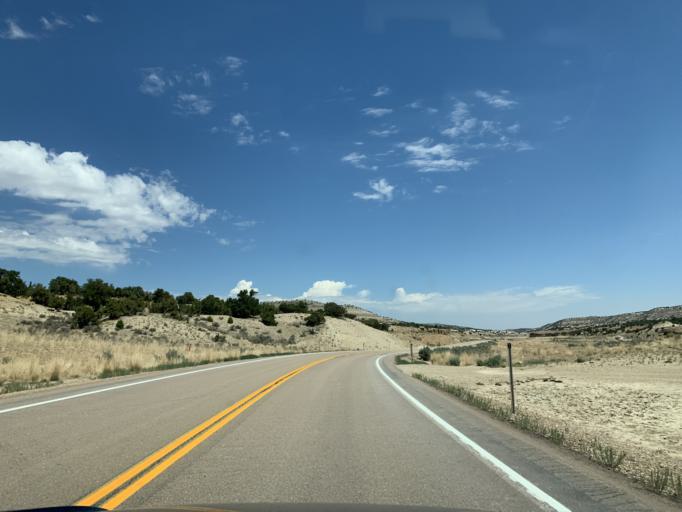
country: US
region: Utah
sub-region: Duchesne County
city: Duchesne
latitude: 39.9374
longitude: -110.2161
